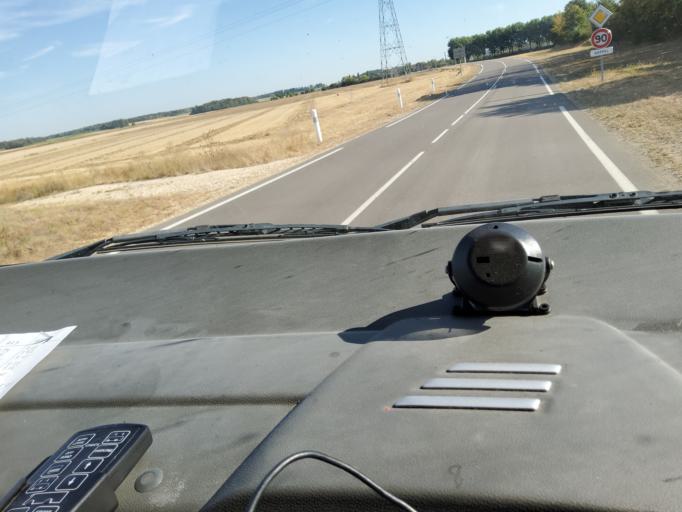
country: FR
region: Bourgogne
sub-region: Departement de la Cote-d'Or
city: Saint-Usage
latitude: 47.1382
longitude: 5.2673
